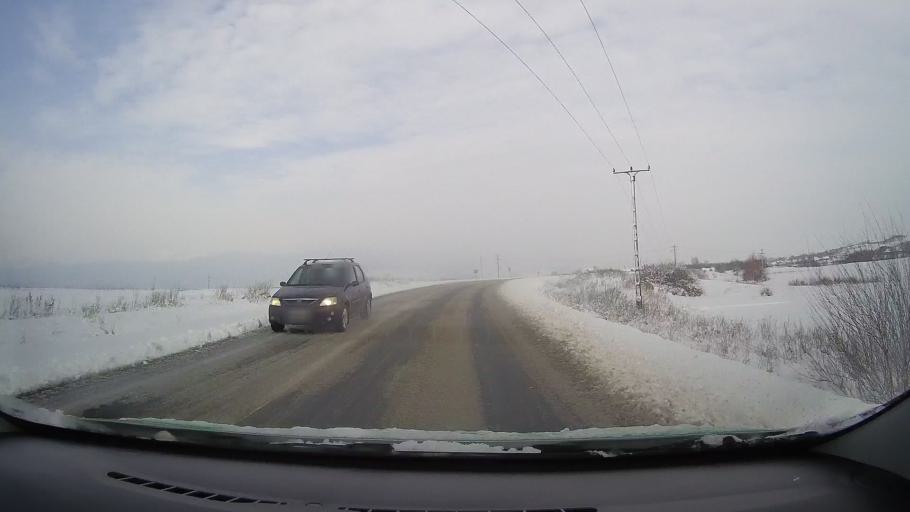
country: RO
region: Alba
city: Vurpar
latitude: 45.9684
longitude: 23.4795
